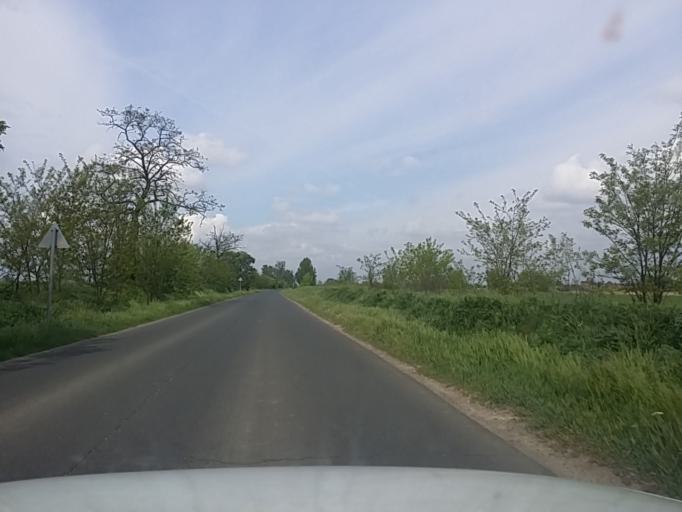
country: HU
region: Pest
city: Szentlorinckata
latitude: 47.5076
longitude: 19.7633
